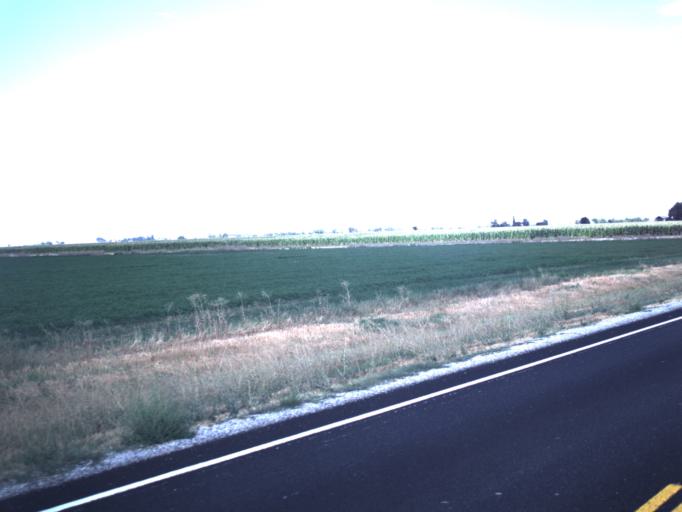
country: US
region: Utah
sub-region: Box Elder County
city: Honeyville
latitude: 41.6240
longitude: -112.1268
